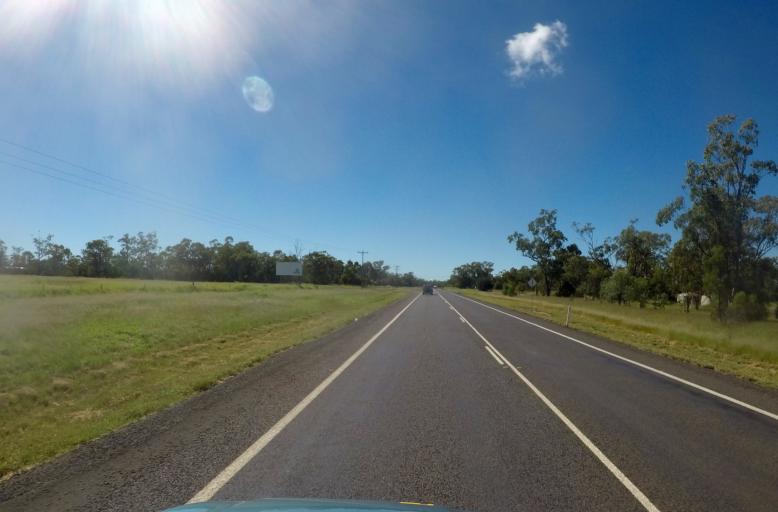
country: AU
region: Queensland
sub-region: Maranoa
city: Roma
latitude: -26.5798
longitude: 148.9560
